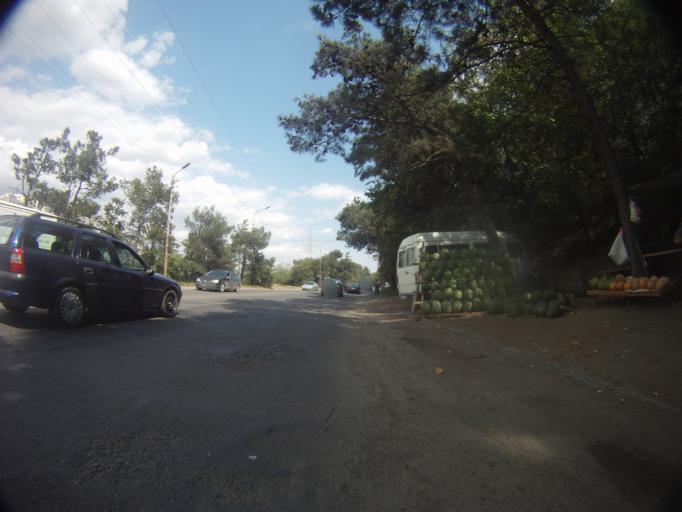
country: GE
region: T'bilisi
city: Tbilisi
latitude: 41.6696
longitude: 44.8540
